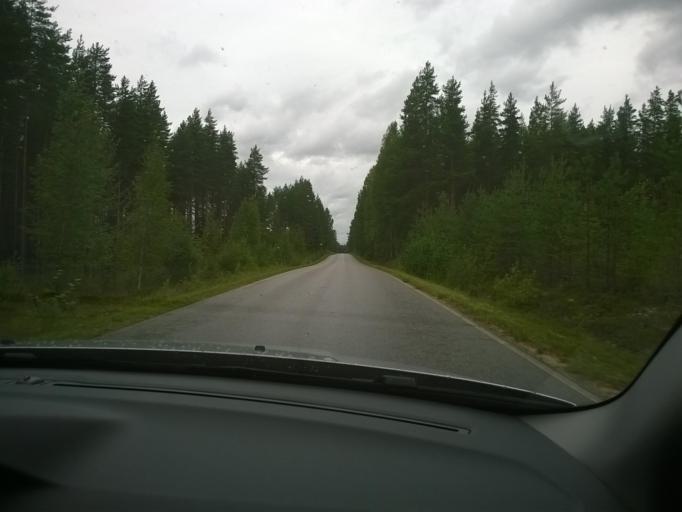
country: FI
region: Kainuu
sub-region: Kehys-Kainuu
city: Kuhmo
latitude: 64.1337
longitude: 29.4359
